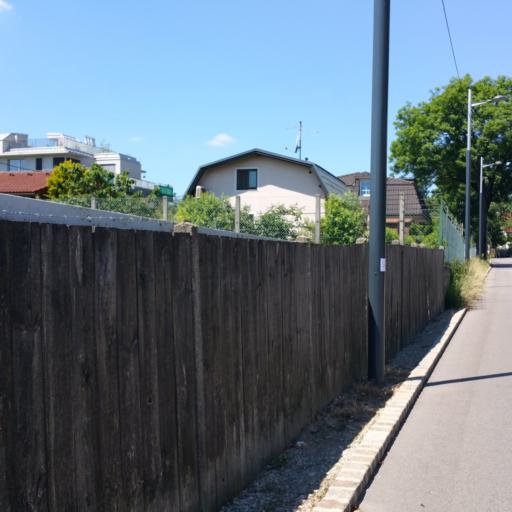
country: AT
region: Vienna
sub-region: Wien Stadt
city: Vienna
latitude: 48.2158
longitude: 16.3000
